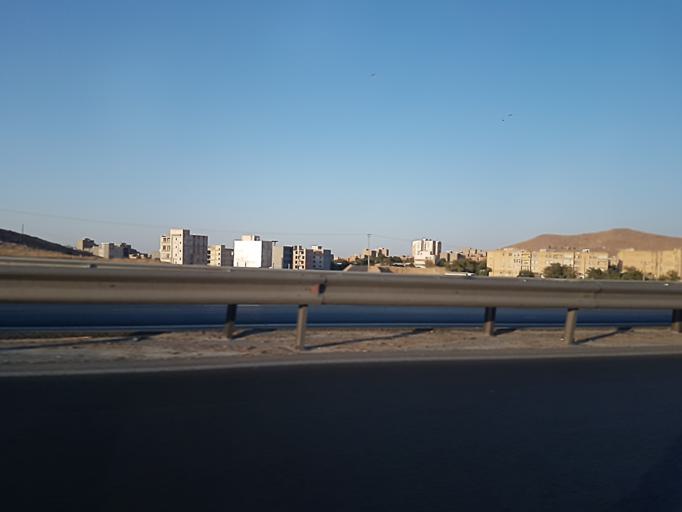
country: IR
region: Markazi
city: Arak
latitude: 34.0692
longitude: 49.7148
